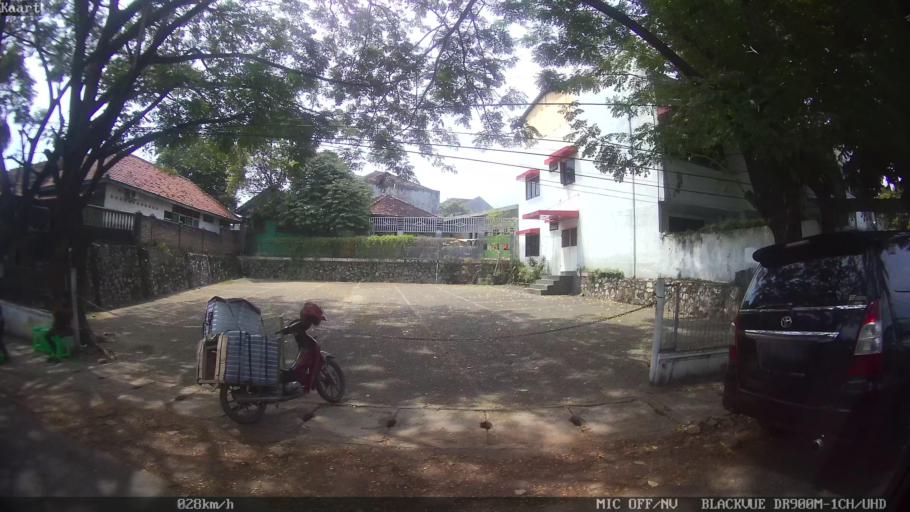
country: ID
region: Lampung
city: Bandarlampung
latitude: -5.4453
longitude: 105.2641
